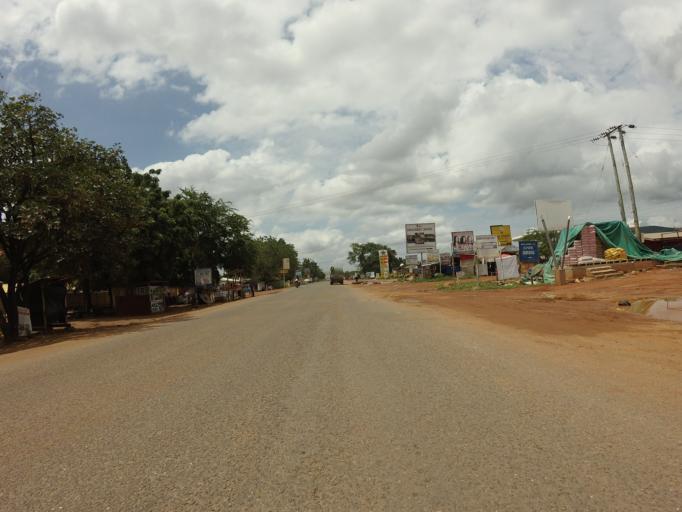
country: GH
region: Eastern
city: Aburi
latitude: 5.8375
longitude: -0.1165
